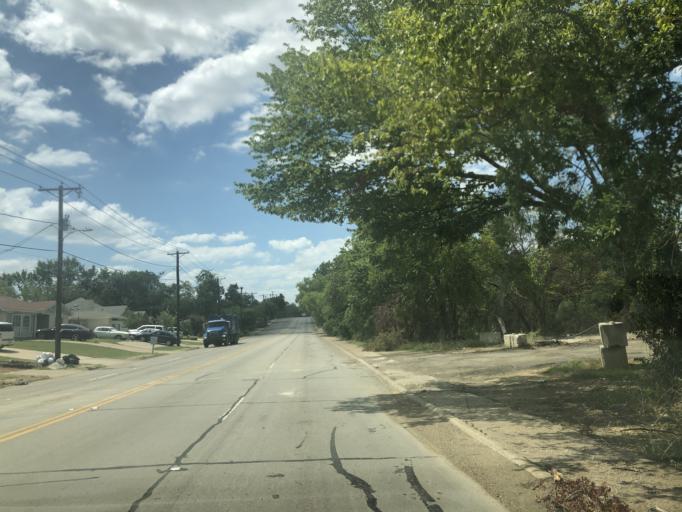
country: US
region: Texas
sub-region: Dallas County
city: Grand Prairie
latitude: 32.7474
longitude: -97.0288
